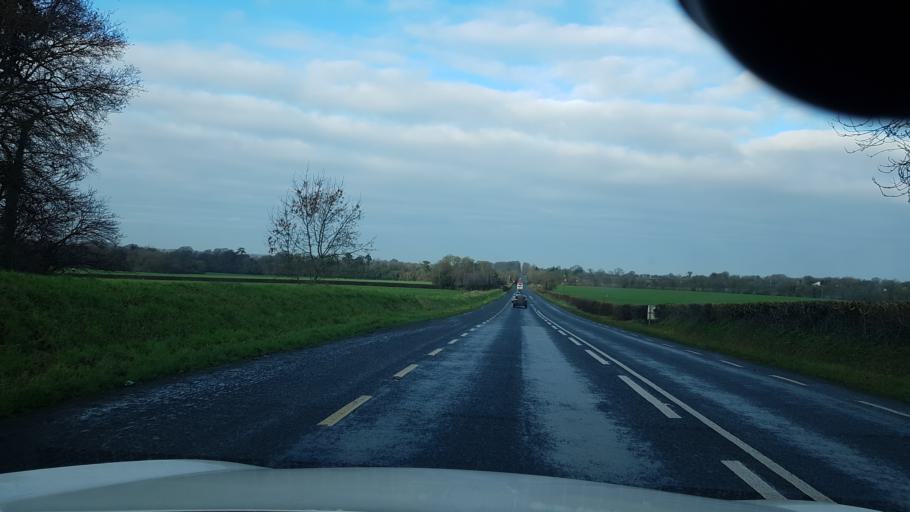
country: IE
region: Leinster
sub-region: An Mhi
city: Navan
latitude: 53.6123
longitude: -6.6325
